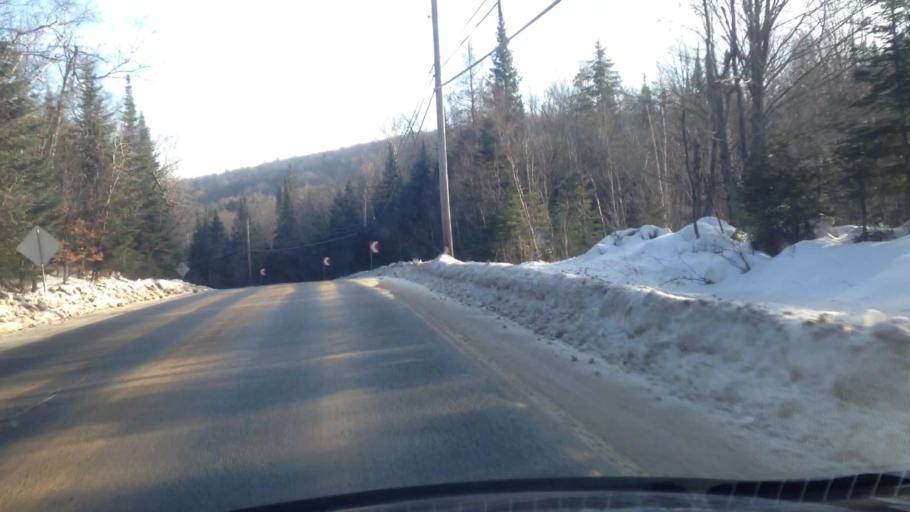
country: CA
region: Quebec
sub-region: Laurentides
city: Sainte-Agathe-des-Monts
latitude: 45.9116
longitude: -74.3565
